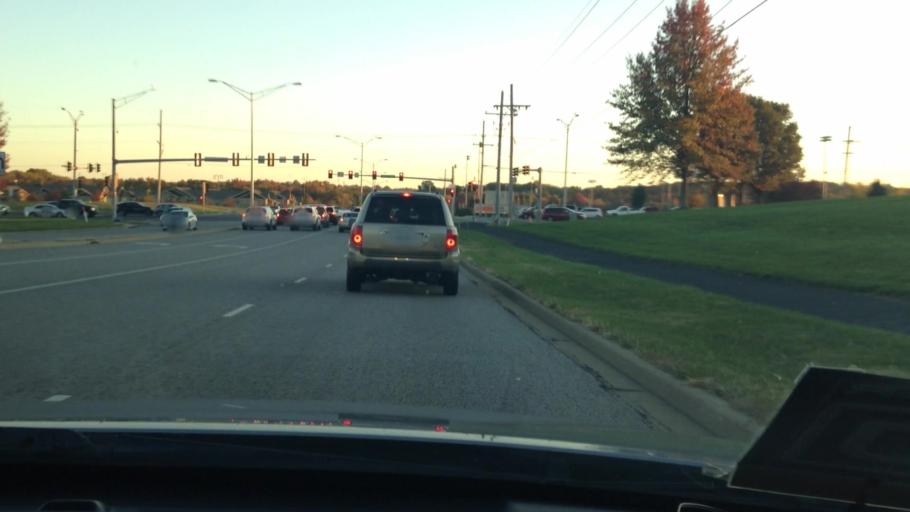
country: US
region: Kansas
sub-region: Johnson County
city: Lenexa
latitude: 38.8848
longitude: -94.7006
